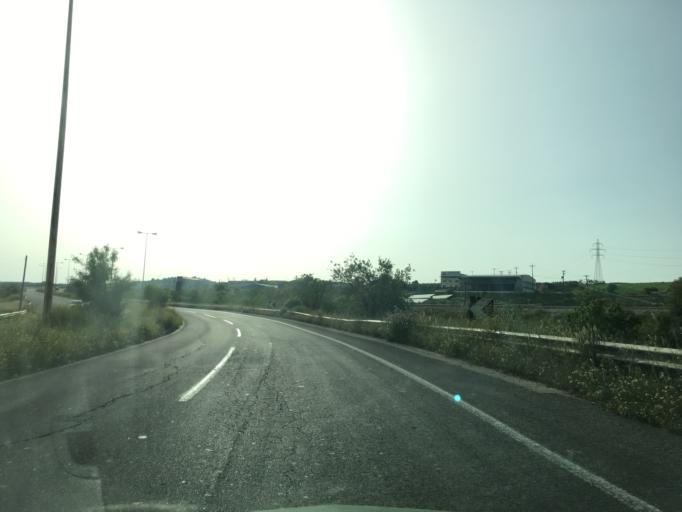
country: GR
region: Thessaly
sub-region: Nomos Magnisias
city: Nea Ionia
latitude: 39.3826
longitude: 22.8607
